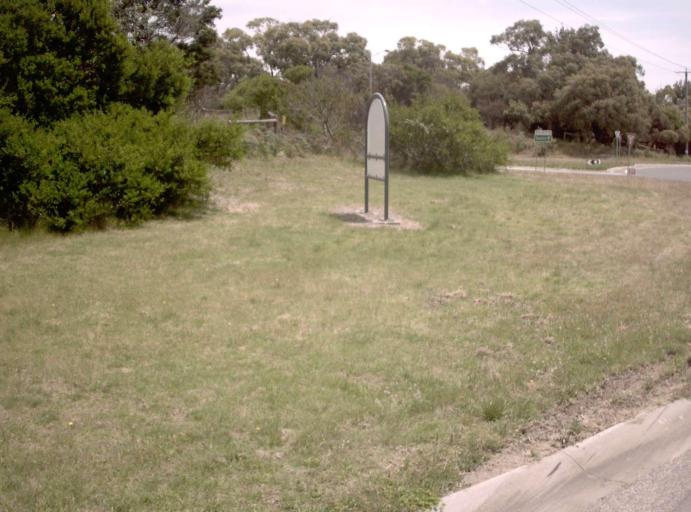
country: AU
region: Victoria
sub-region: Casey
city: Cranbourne South
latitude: -38.1223
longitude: 145.2304
